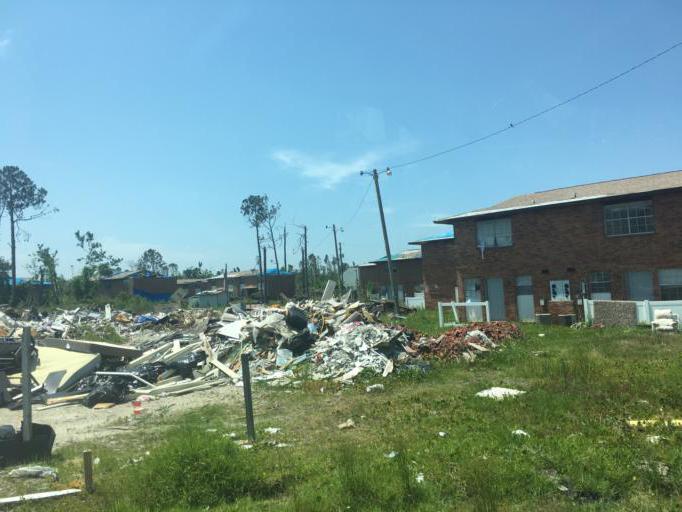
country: US
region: Florida
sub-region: Bay County
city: Lynn Haven
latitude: 30.2204
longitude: -85.6473
